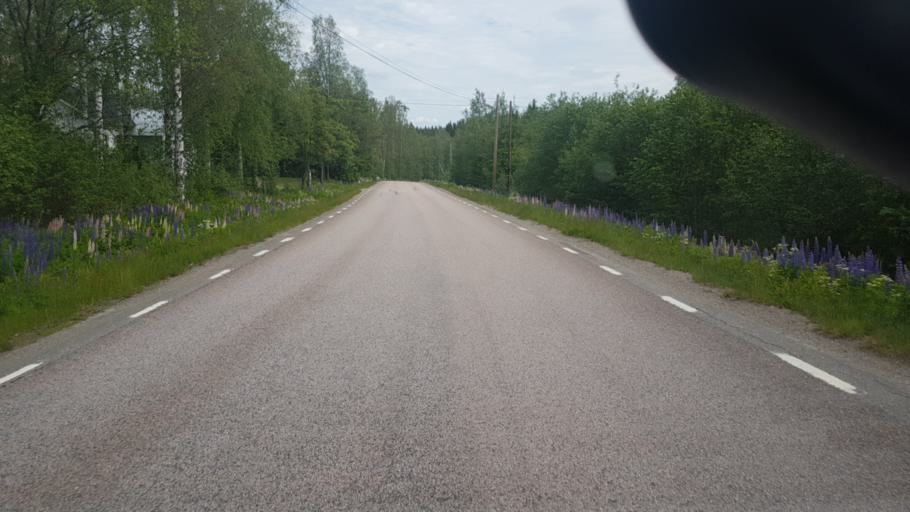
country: SE
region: Vaermland
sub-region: Eda Kommun
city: Amotfors
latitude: 59.8662
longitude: 12.4437
